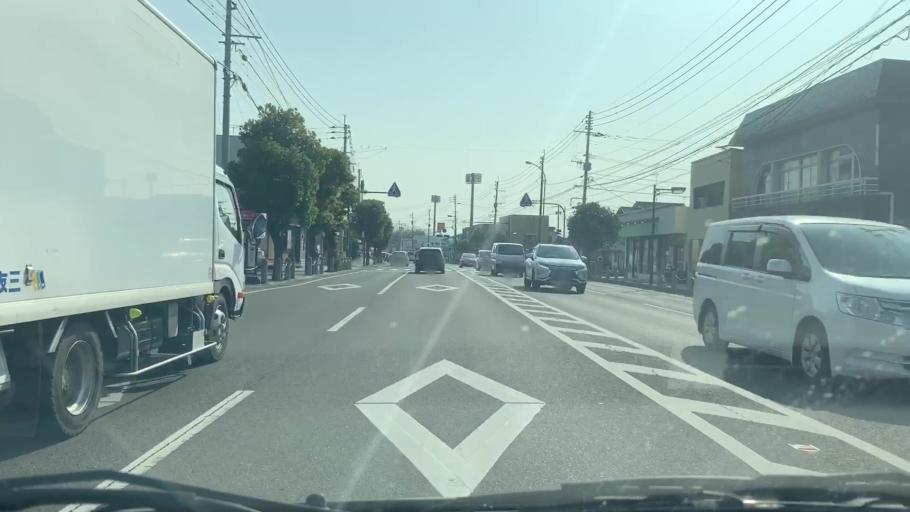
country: JP
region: Saga Prefecture
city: Saga-shi
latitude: 33.2811
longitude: 130.2921
